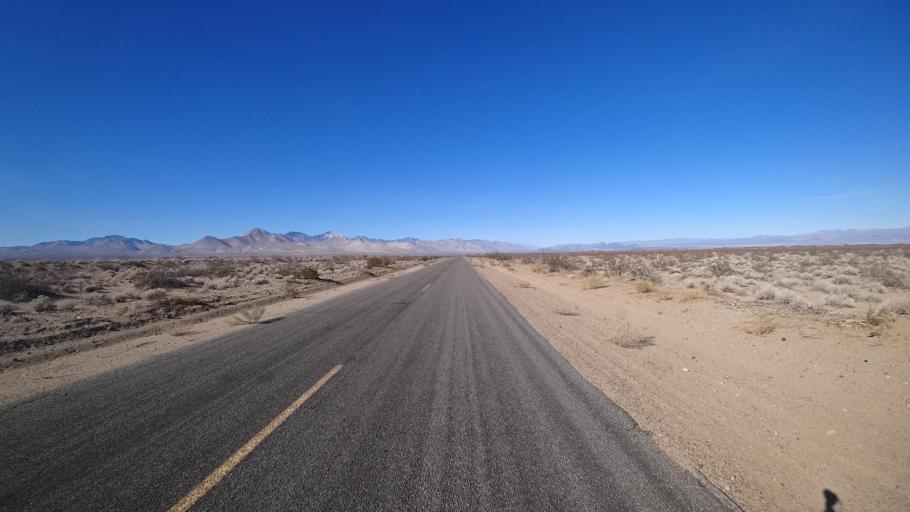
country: US
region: California
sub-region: Kern County
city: China Lake Acres
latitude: 35.5826
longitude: -117.7884
